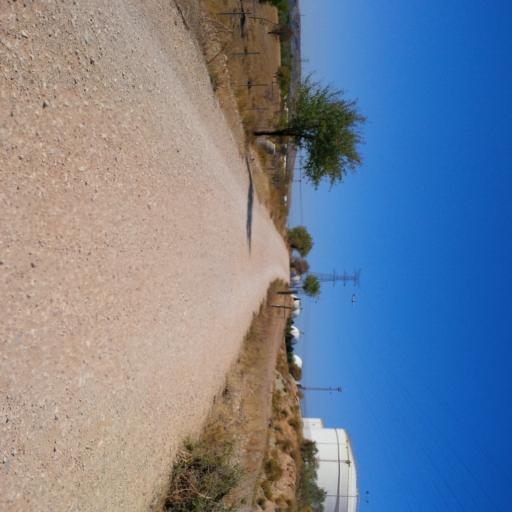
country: ES
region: Madrid
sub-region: Provincia de Madrid
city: Torrejon de Ardoz
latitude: 40.4301
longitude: -3.4841
